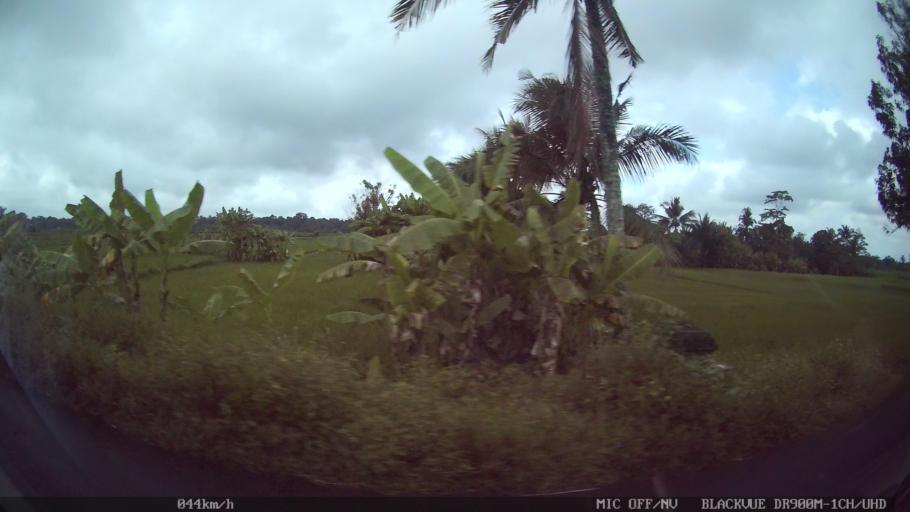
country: ID
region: Bali
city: Banjar Teguan
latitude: -8.5017
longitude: 115.2254
